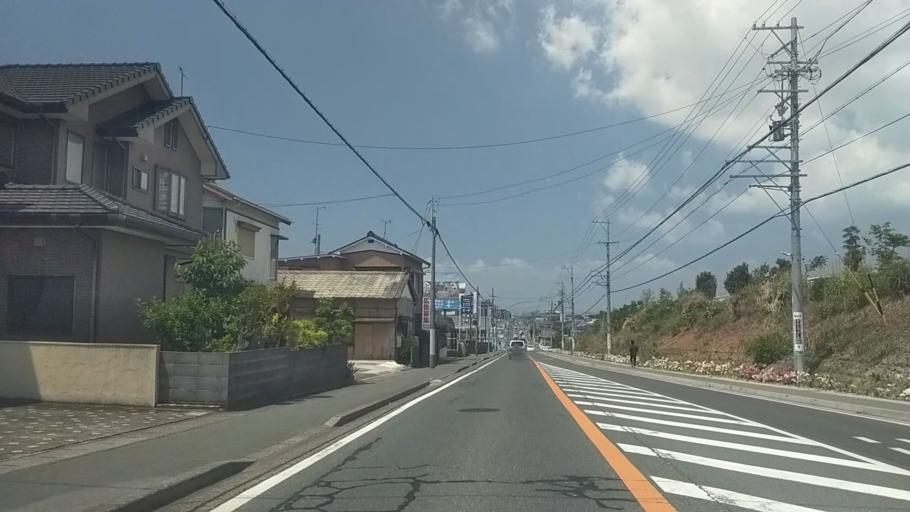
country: JP
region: Shizuoka
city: Hamamatsu
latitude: 34.7362
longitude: 137.7197
